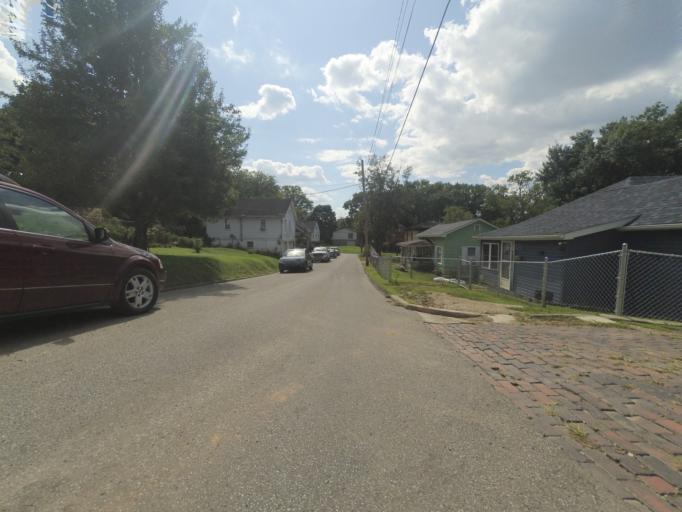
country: US
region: West Virginia
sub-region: Cabell County
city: Huntington
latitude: 38.4111
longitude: -82.4226
